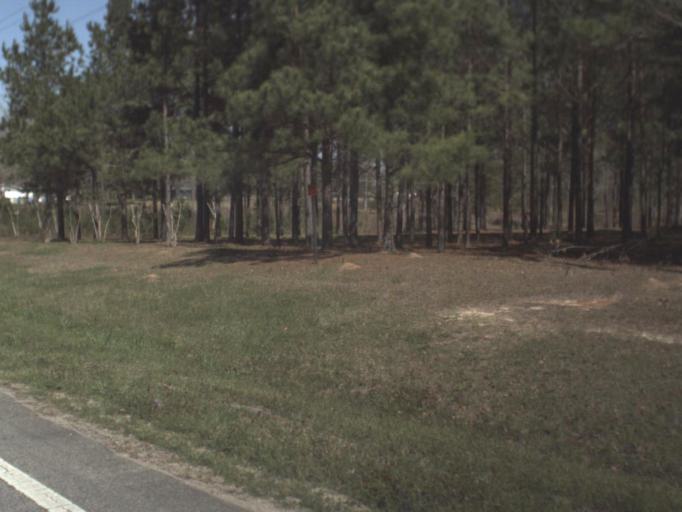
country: US
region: Florida
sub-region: Gadsden County
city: Gretna
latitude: 30.6759
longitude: -84.6175
